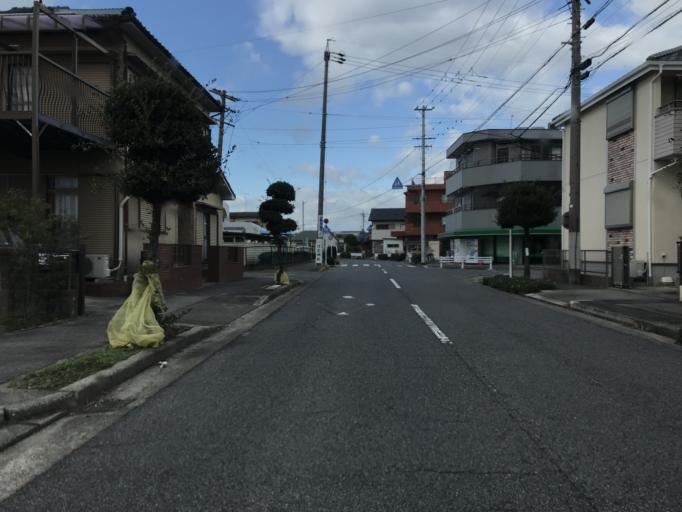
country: JP
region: Aichi
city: Nagoya-shi
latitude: 35.2083
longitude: 136.8427
